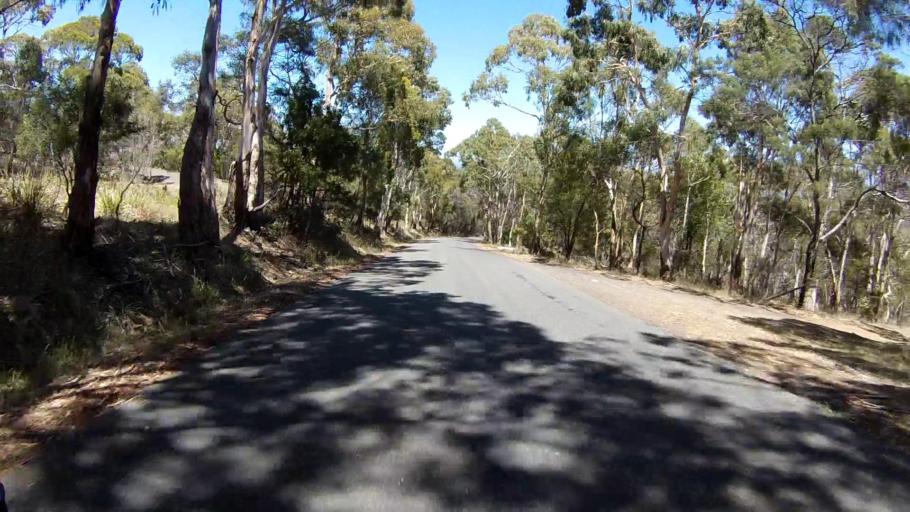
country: AU
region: Tasmania
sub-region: Clarence
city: Cambridge
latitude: -42.8492
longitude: 147.4306
